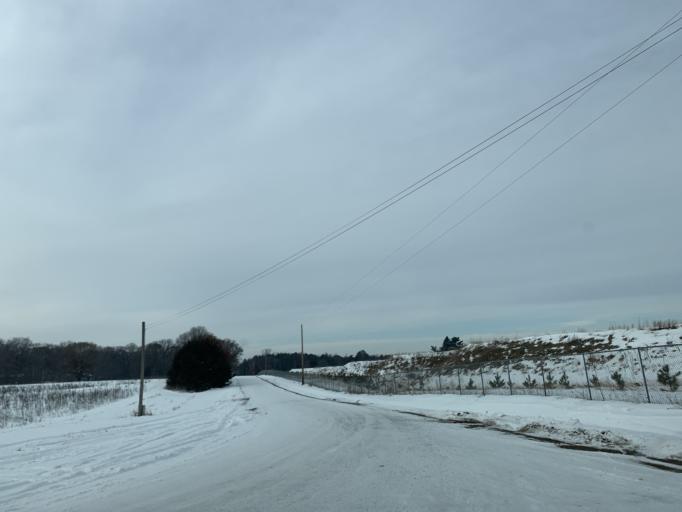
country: US
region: Minnesota
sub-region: Washington County
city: Forest Lake
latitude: 45.2968
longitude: -93.0038
